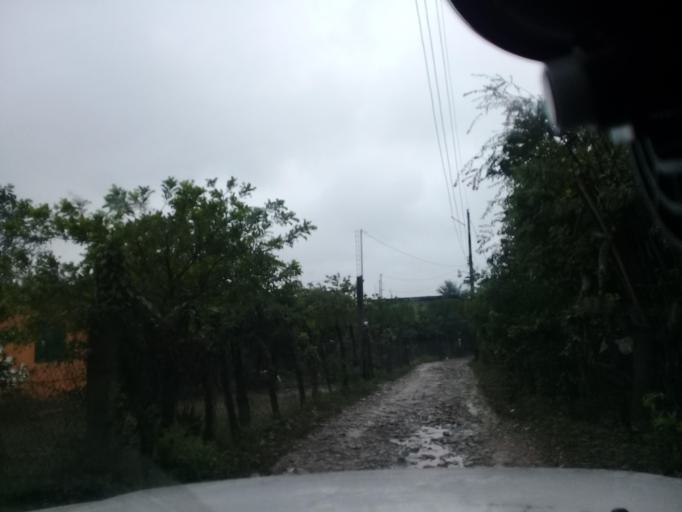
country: MX
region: Veracruz
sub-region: Chalma
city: San Pedro Coyutla
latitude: 21.1845
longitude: -98.4345
